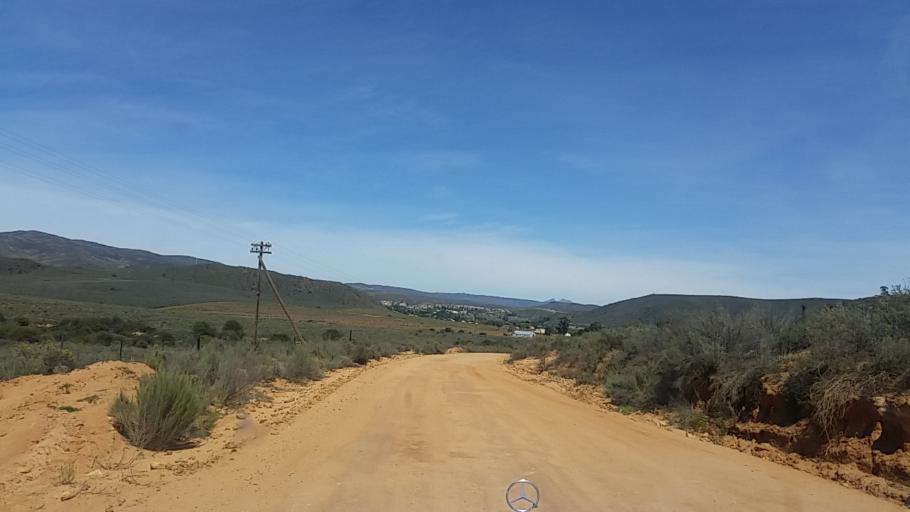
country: ZA
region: Western Cape
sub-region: Eden District Municipality
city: Knysna
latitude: -33.6380
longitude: 23.1510
